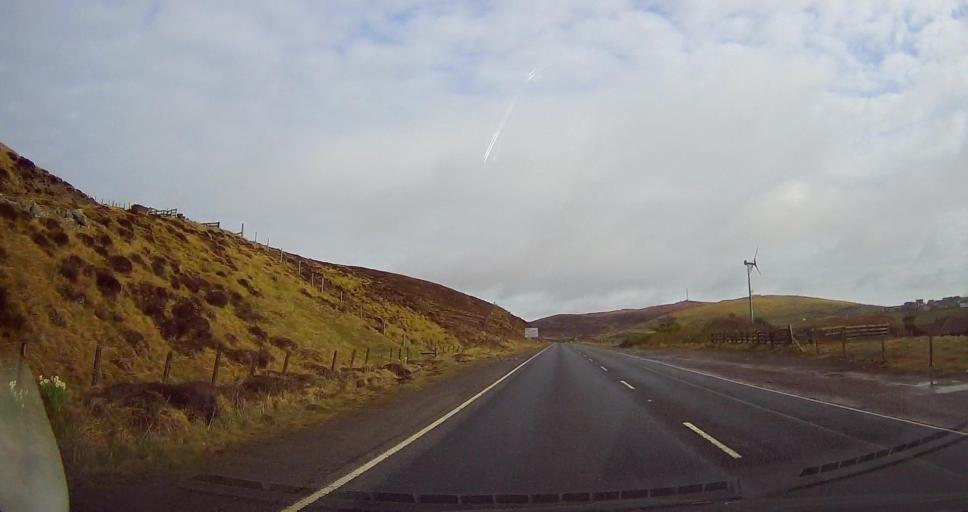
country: GB
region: Scotland
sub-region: Shetland Islands
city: Lerwick
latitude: 60.1321
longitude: -1.2148
